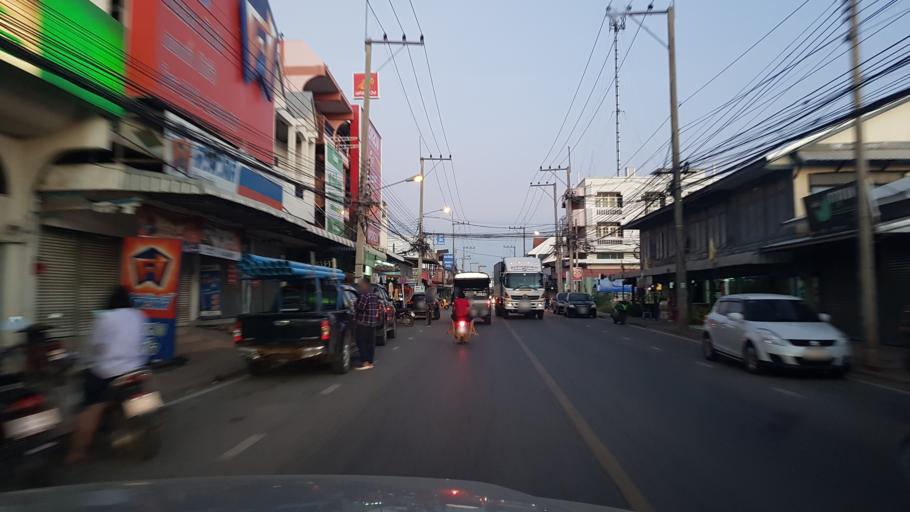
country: TH
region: Chaiyaphum
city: Phu Khiao
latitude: 16.3662
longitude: 102.1348
